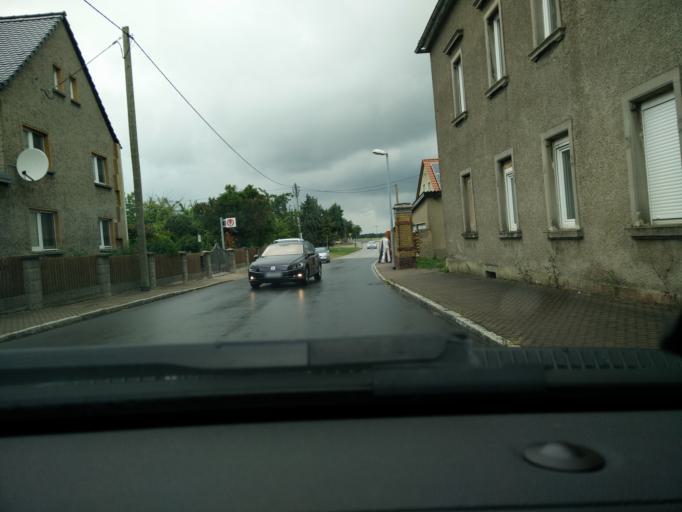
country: DE
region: Saxony
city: Bad Lausick
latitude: 51.1392
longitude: 12.6879
